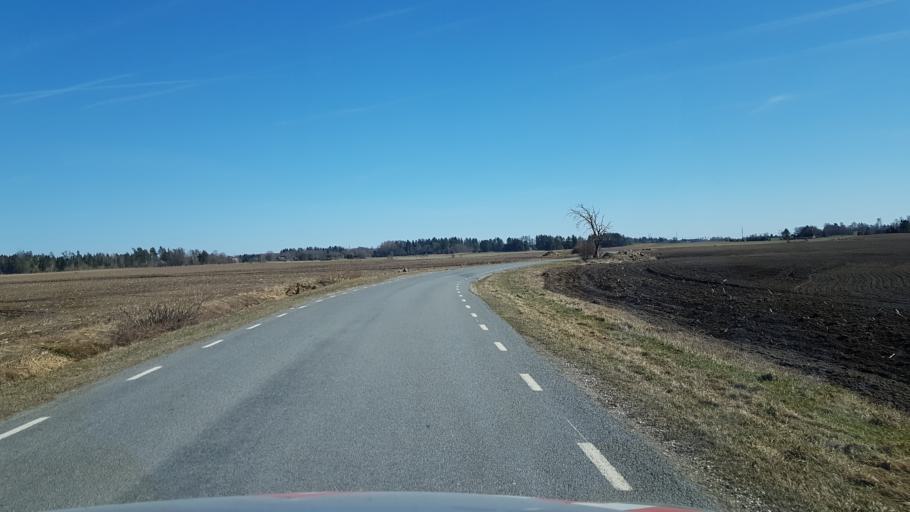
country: EE
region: Laeaene-Virumaa
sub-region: Someru vald
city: Someru
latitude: 59.3374
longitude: 26.5208
